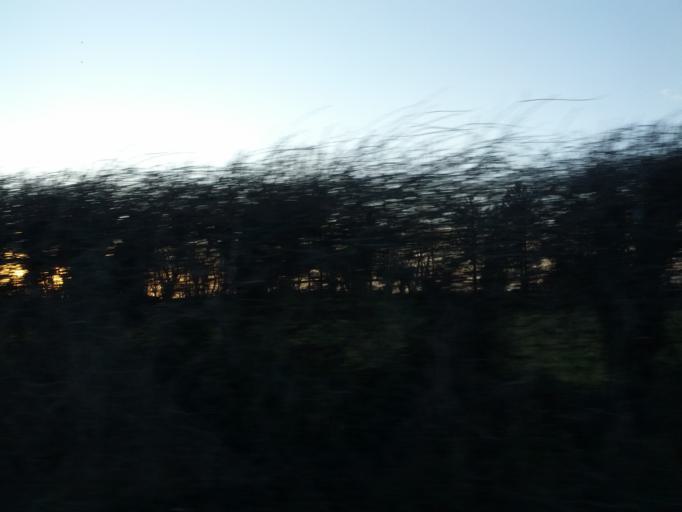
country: IE
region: Connaught
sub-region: County Galway
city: Loughrea
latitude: 53.2774
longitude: -8.6346
